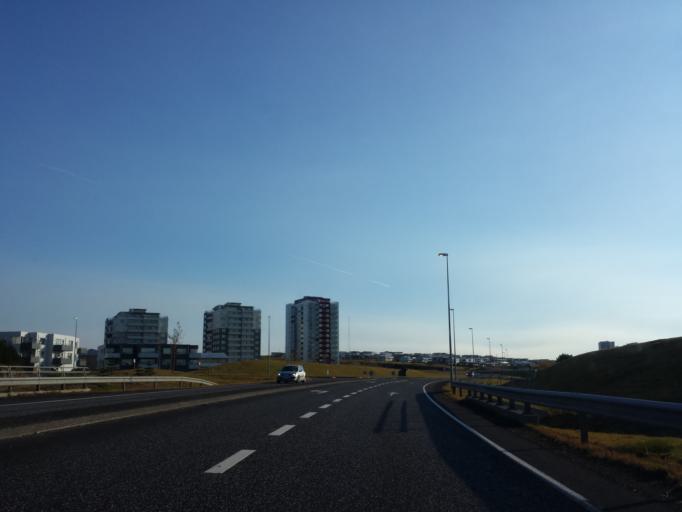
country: IS
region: Capital Region
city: Reykjavik
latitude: 64.0894
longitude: -21.8459
